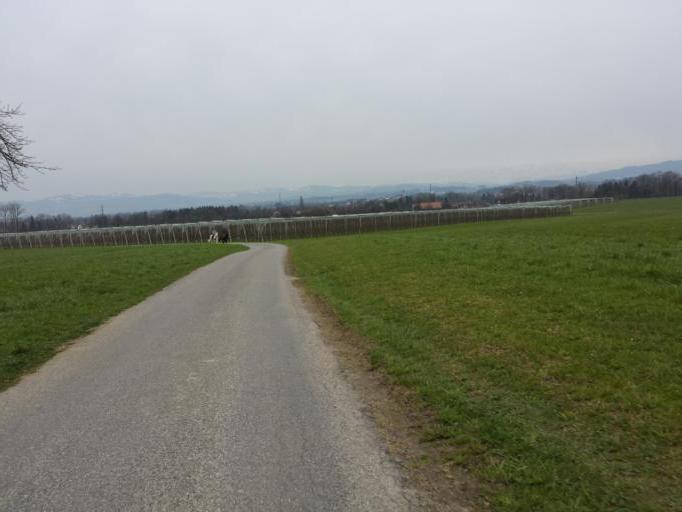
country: CH
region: Thurgau
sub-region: Arbon District
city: Salmsach
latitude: 47.5573
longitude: 9.3466
